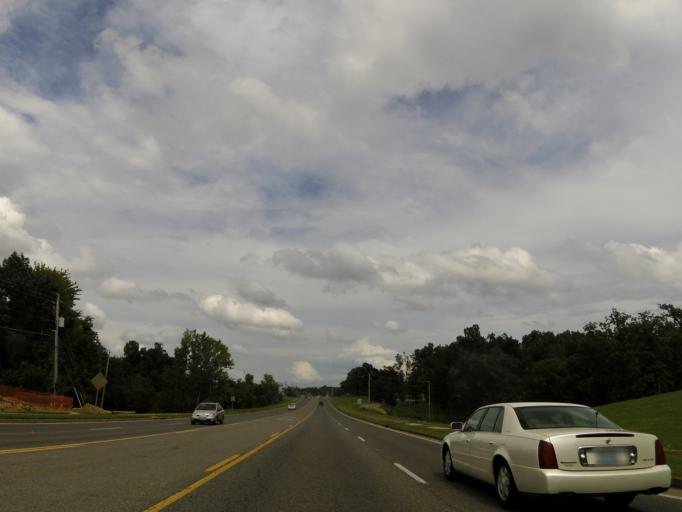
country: US
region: Kentucky
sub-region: McCracken County
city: Hendron
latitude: 37.0544
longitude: -88.6650
